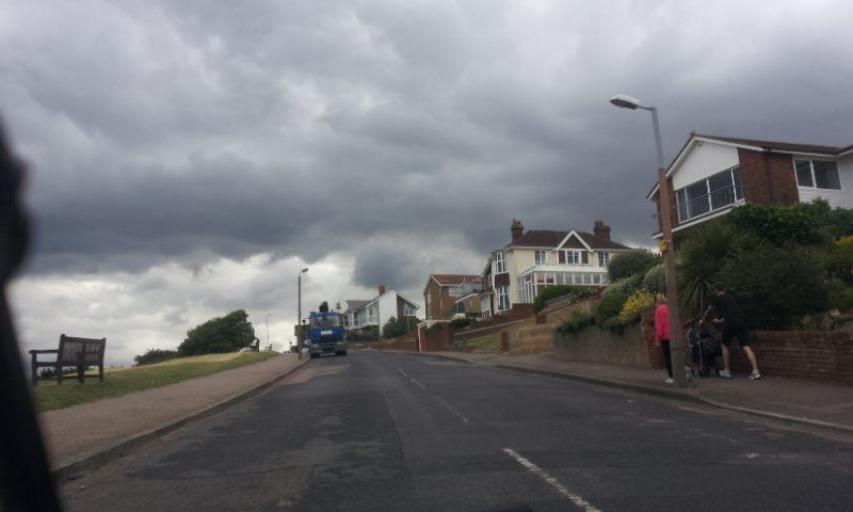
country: GB
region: England
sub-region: Kent
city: Herne Bay
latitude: 51.3718
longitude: 1.1005
